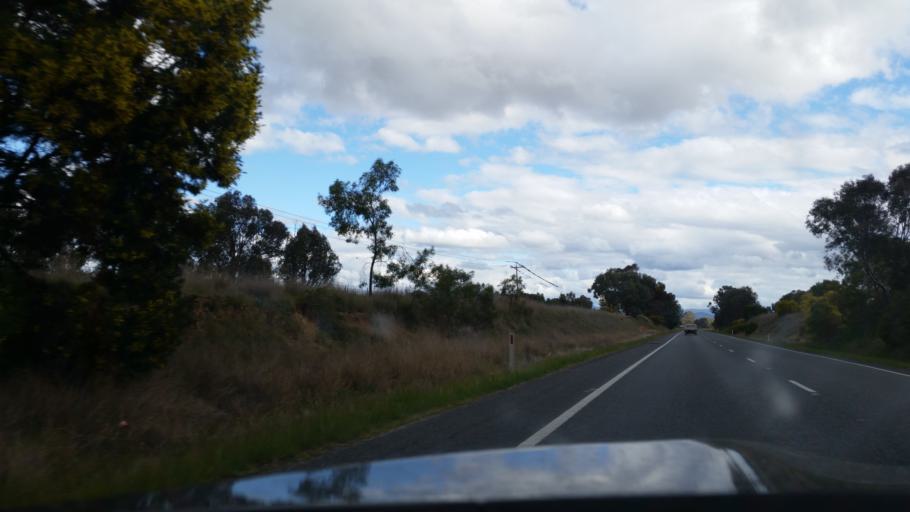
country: AU
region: New South Wales
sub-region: Albury Municipality
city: Lavington
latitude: -35.9859
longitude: 146.9979
